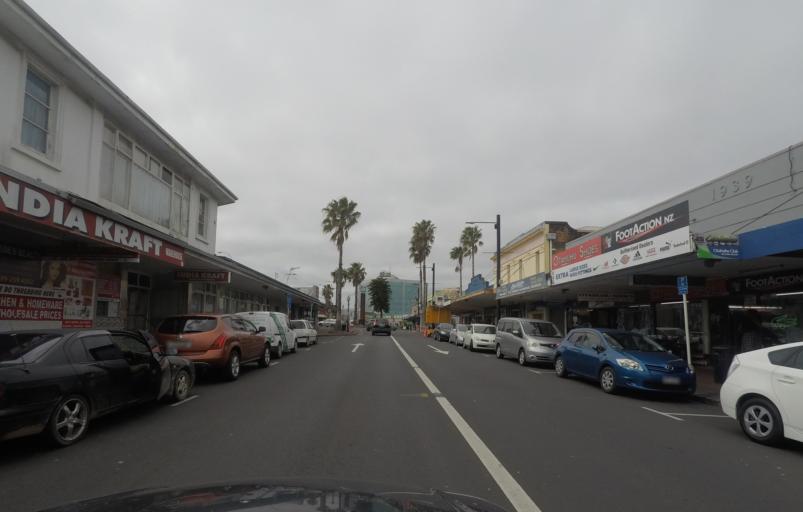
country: NZ
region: Auckland
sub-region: Auckland
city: Mangere
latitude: -36.9449
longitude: 174.8444
